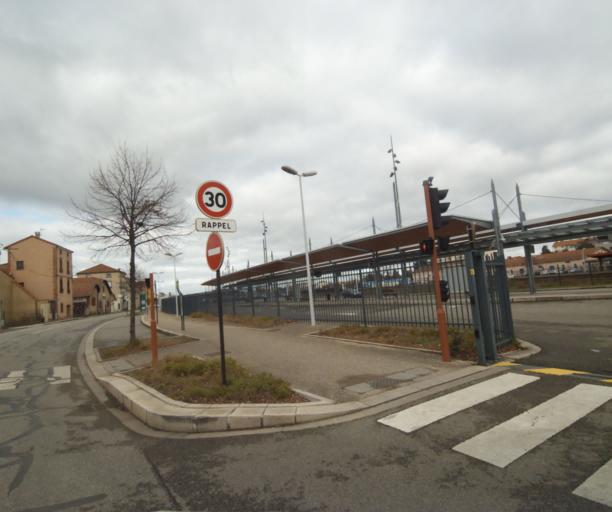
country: FR
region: Rhone-Alpes
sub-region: Departement de la Loire
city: Roanne
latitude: 46.0390
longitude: 4.0619
